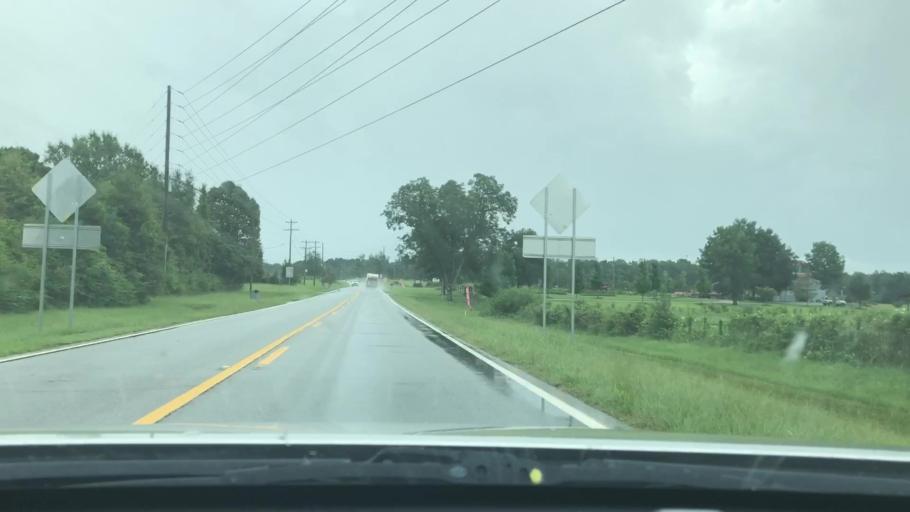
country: US
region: Georgia
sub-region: Lamar County
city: Barnesville
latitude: 33.0606
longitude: -84.2067
